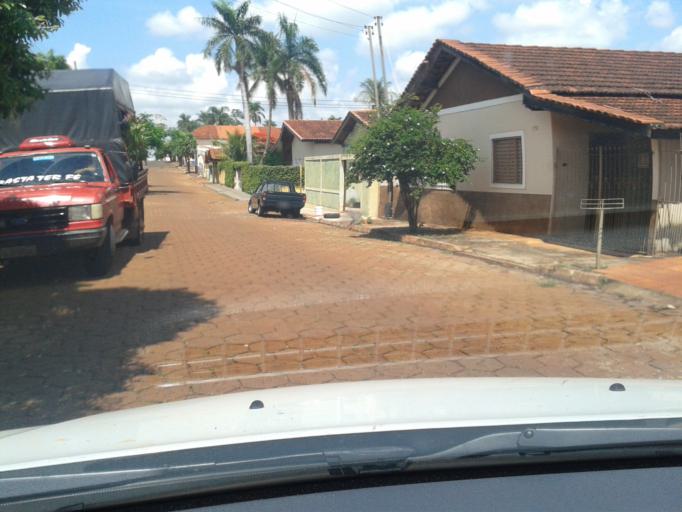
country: BR
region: Minas Gerais
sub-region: Centralina
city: Centralina
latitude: -18.5841
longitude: -49.1961
